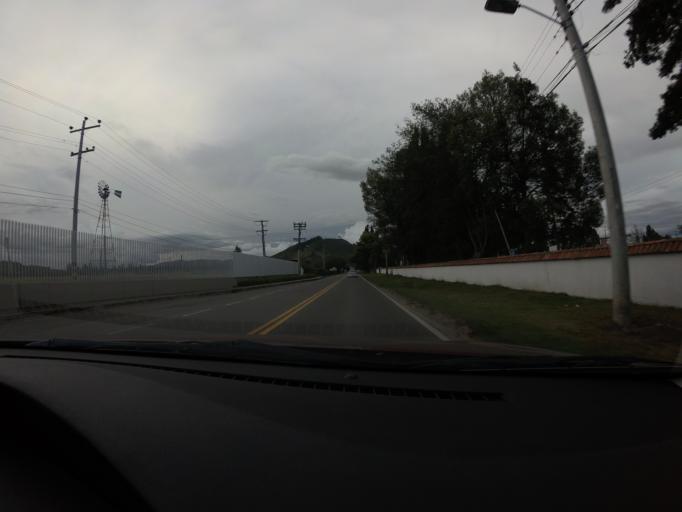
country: CO
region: Cundinamarca
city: Sopo
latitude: 4.9347
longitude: -73.9555
